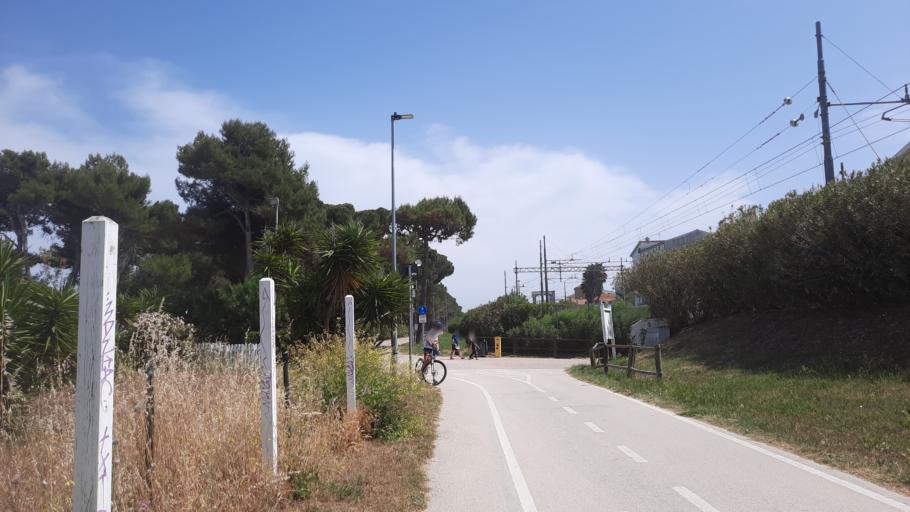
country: IT
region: Abruzzo
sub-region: Provincia di Teramo
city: Pineto
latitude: 42.6106
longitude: 14.0671
